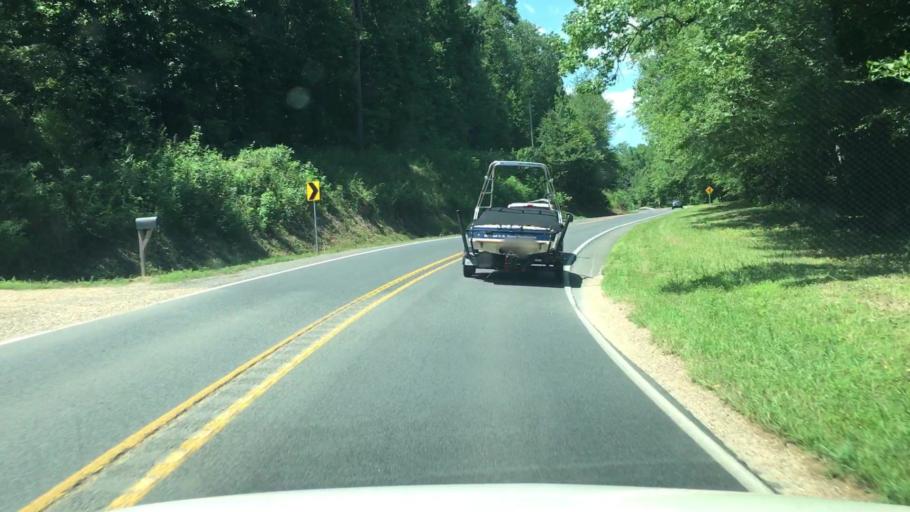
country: US
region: Arkansas
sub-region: Garland County
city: Lake Hamilton
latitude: 34.3418
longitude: -93.1839
